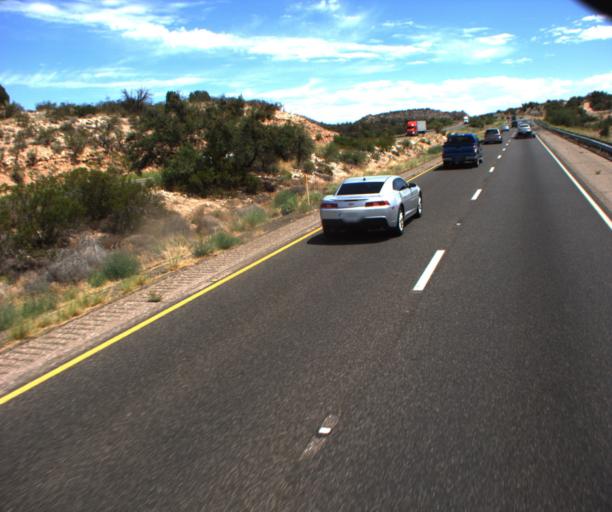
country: US
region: Arizona
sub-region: Yavapai County
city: Lake Montezuma
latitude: 34.6519
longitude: -111.7974
